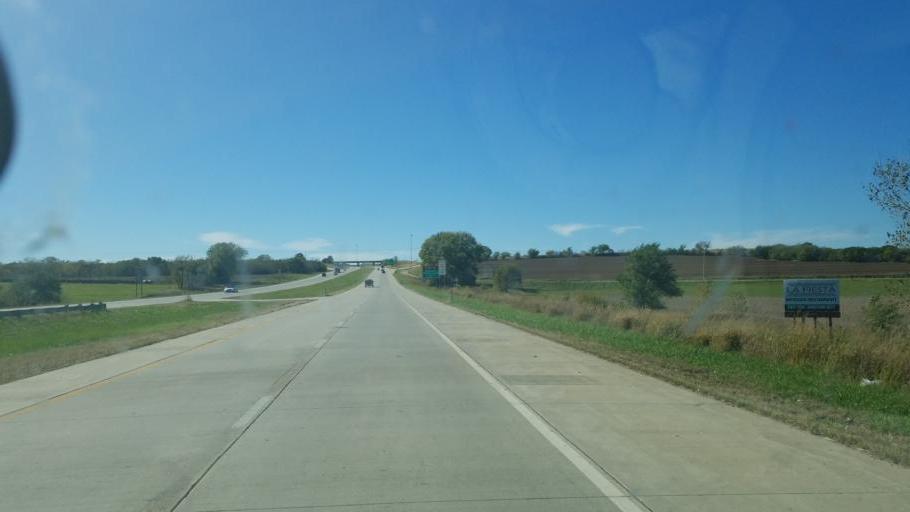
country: US
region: Kansas
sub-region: Riley County
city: Ogden
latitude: 39.0611
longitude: -96.7312
